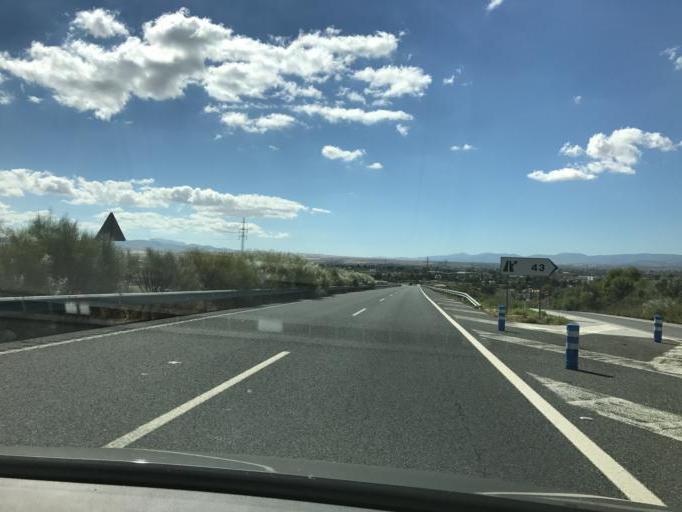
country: ES
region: Andalusia
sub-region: Provincia de Granada
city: Baza
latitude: 37.5077
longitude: -2.7716
